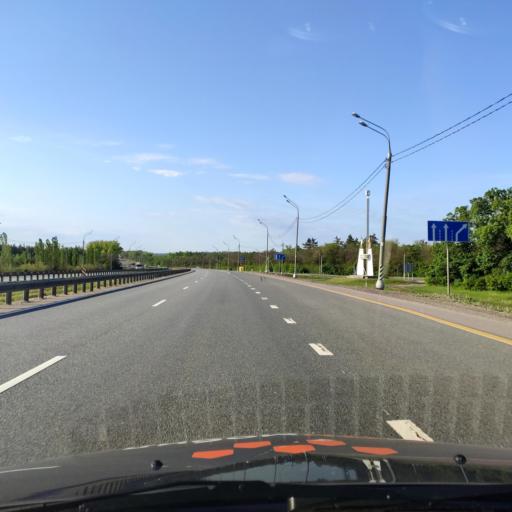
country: RU
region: Lipetsk
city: Khlevnoye
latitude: 52.0980
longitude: 39.1759
